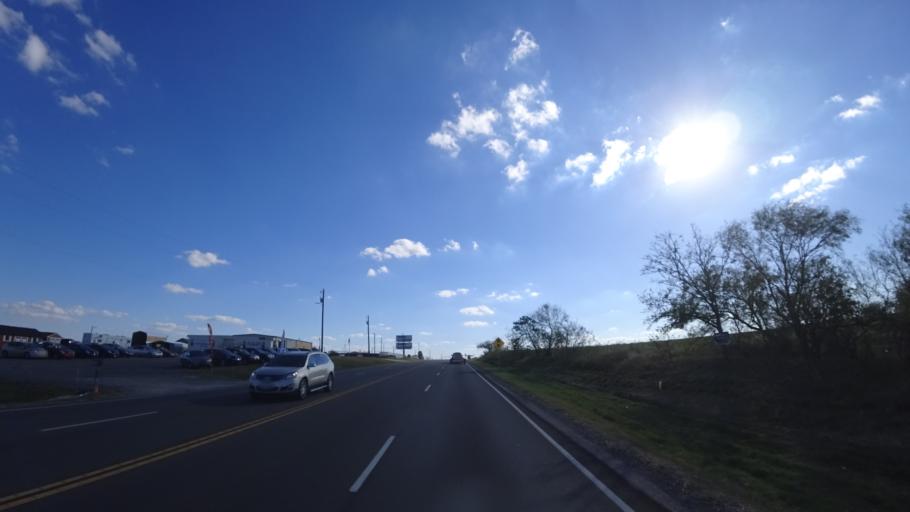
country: US
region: Texas
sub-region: Travis County
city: Onion Creek
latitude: 30.0981
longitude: -97.6942
